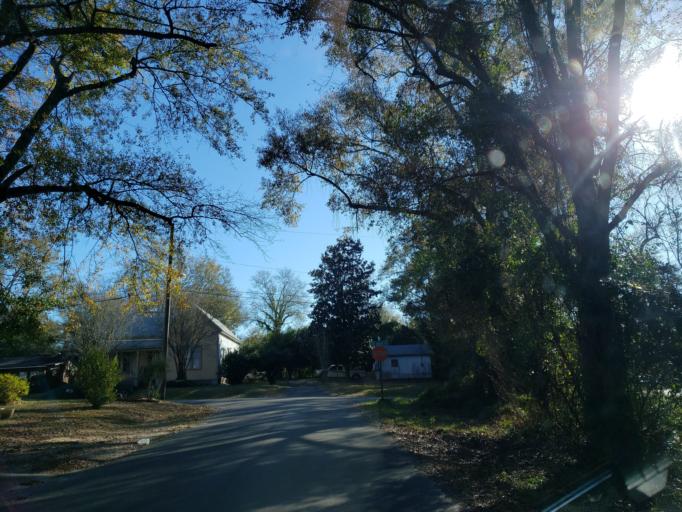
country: US
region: Mississippi
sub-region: Forrest County
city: Hattiesburg
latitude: 31.3270
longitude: -89.3003
